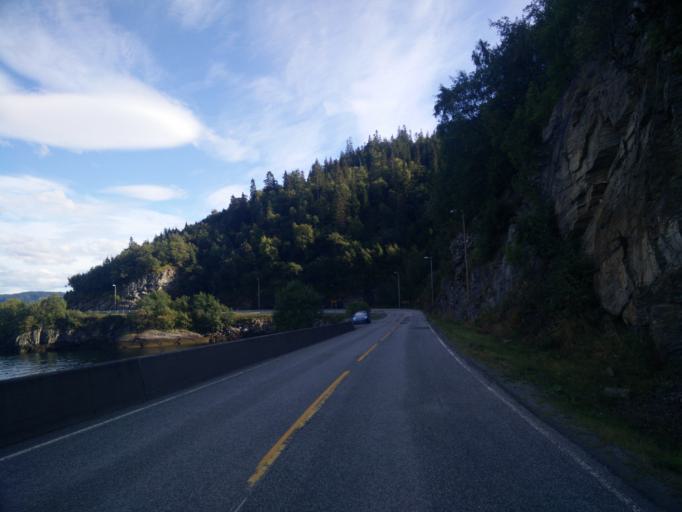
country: NO
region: Sor-Trondelag
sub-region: Skaun
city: Borsa
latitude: 63.3287
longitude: 10.1022
